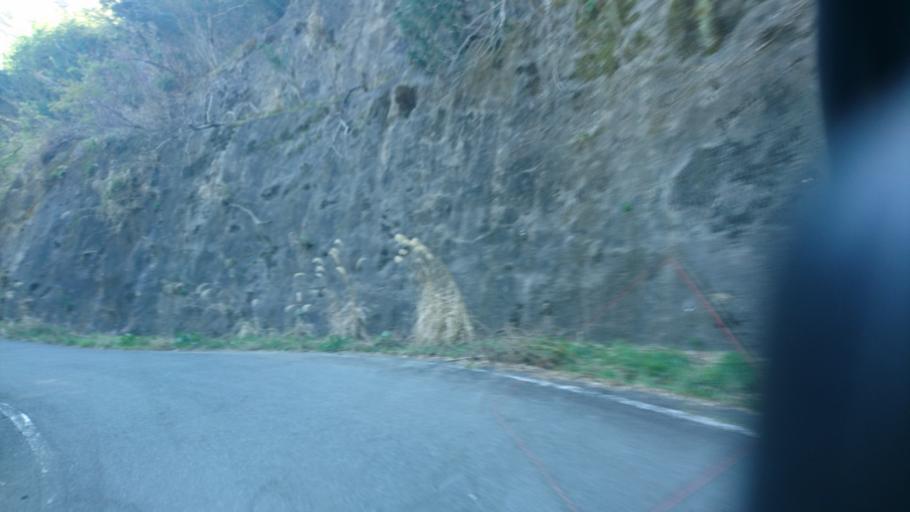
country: JP
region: Shizuoka
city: Fujinomiya
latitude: 35.3326
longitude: 138.4404
